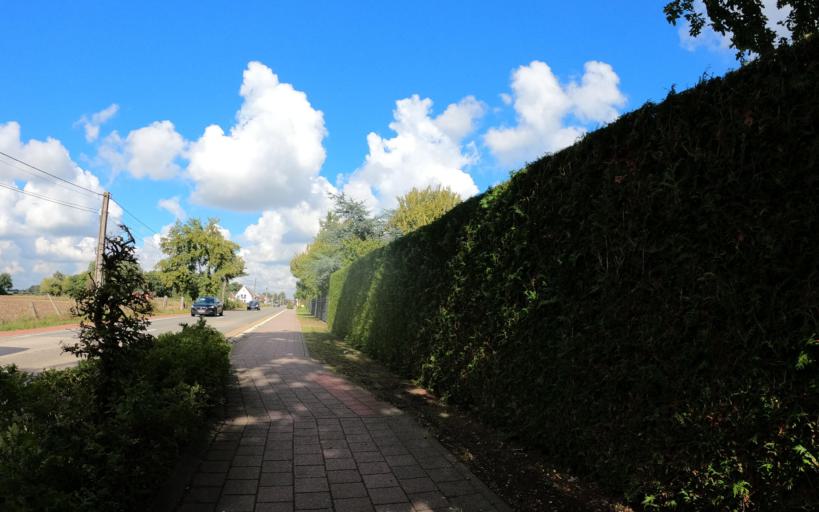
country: BE
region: Flanders
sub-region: Provincie Antwerpen
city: Rijkevorsel
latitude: 51.3147
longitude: 4.7764
